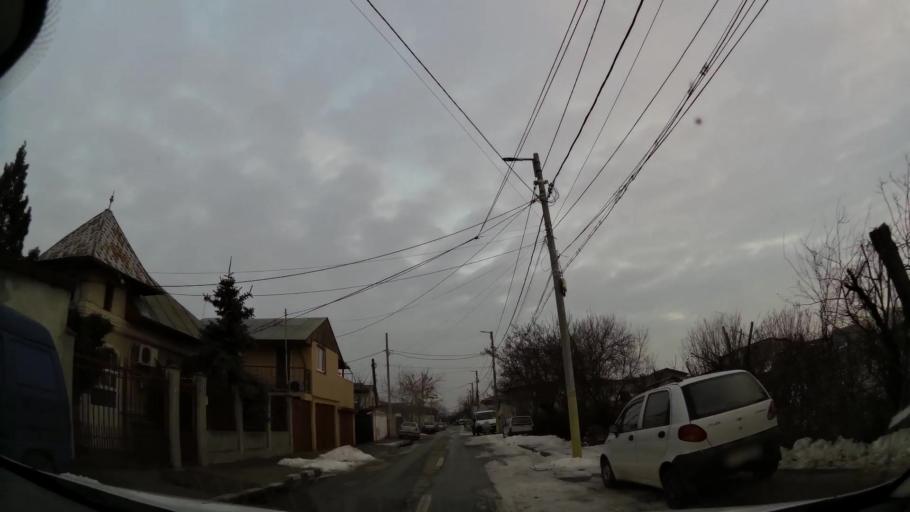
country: RO
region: Ilfov
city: Dobroesti
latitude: 44.4570
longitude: 26.1833
